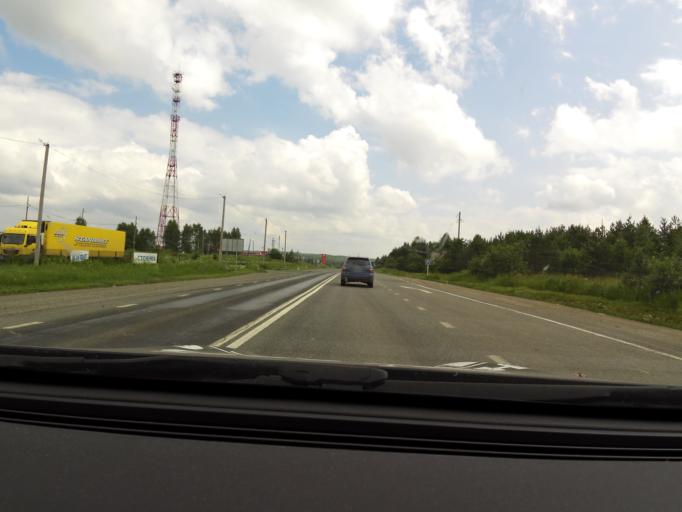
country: RU
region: Sverdlovsk
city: Achit
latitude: 56.8585
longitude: 57.7002
